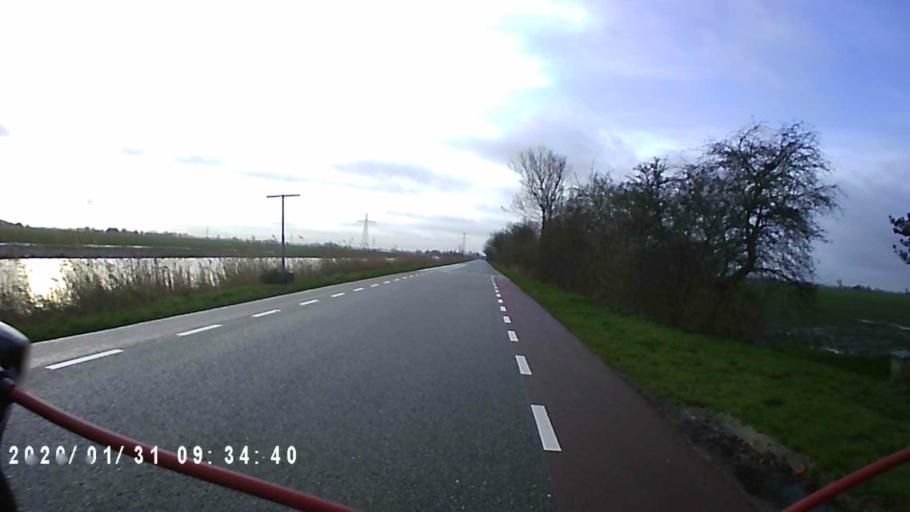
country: NL
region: Groningen
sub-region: Gemeente Winsum
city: Winsum
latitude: 53.3057
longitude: 6.4802
